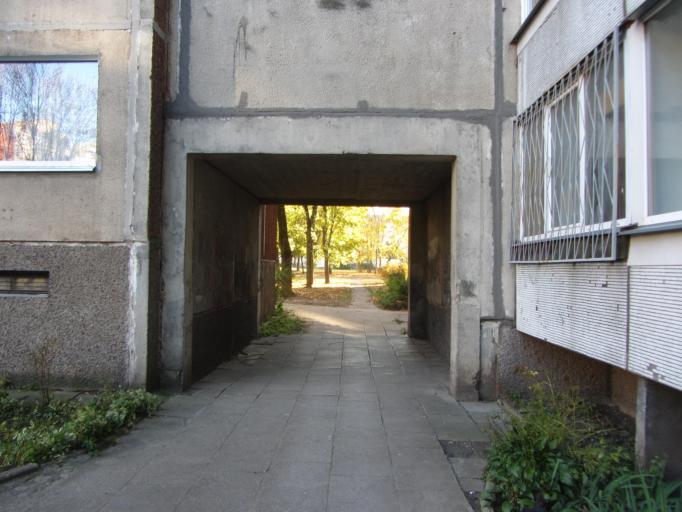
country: LT
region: Vilnius County
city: Lazdynai
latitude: 54.6881
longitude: 25.2034
